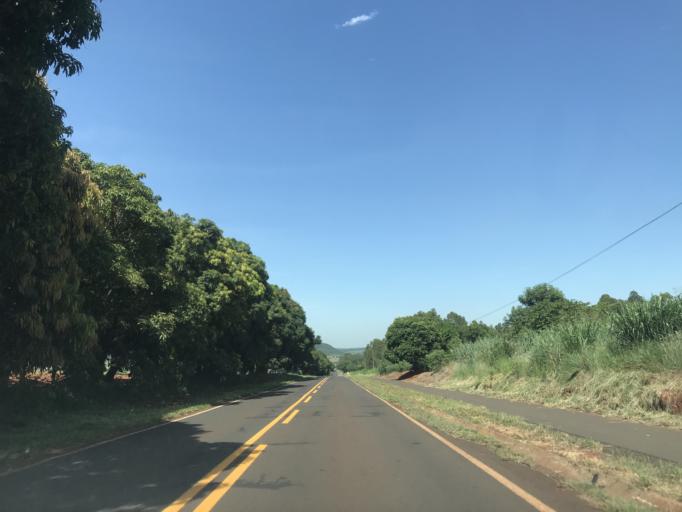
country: BR
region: Parana
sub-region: Terra Rica
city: Terra Rica
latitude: -22.7549
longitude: -52.6282
